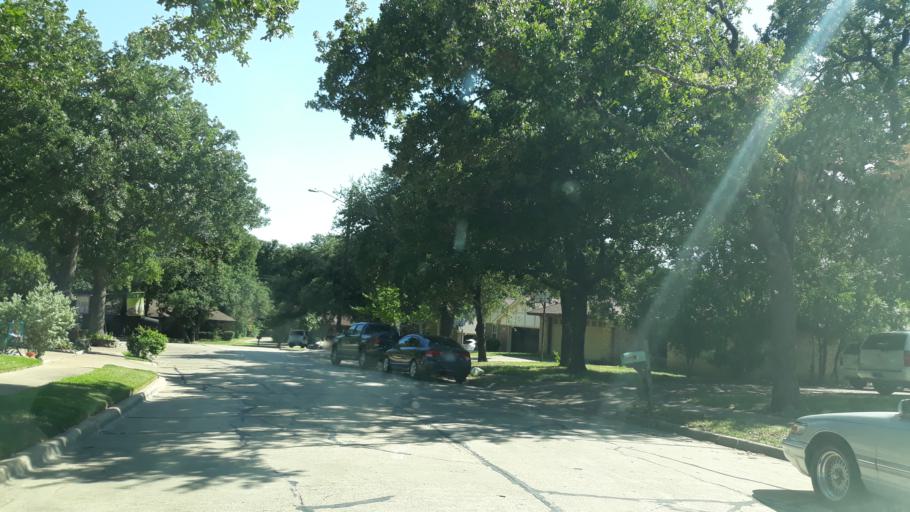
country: US
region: Texas
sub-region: Dallas County
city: Irving
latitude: 32.8297
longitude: -97.0026
